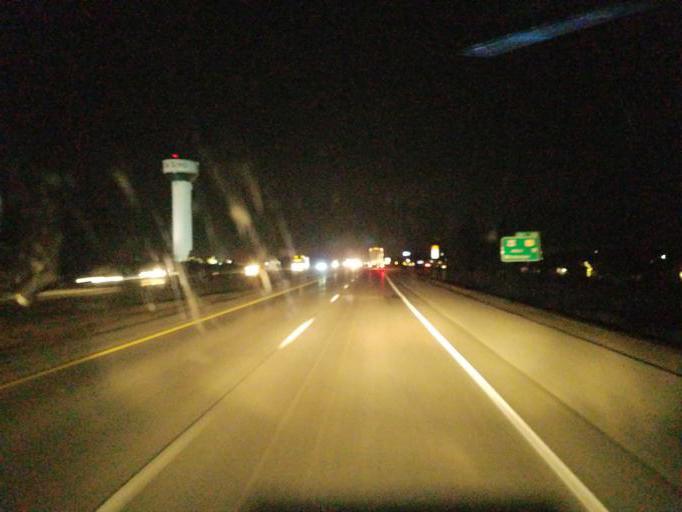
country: US
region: Iowa
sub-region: Dallas County
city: De Soto
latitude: 41.5393
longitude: -94.0198
